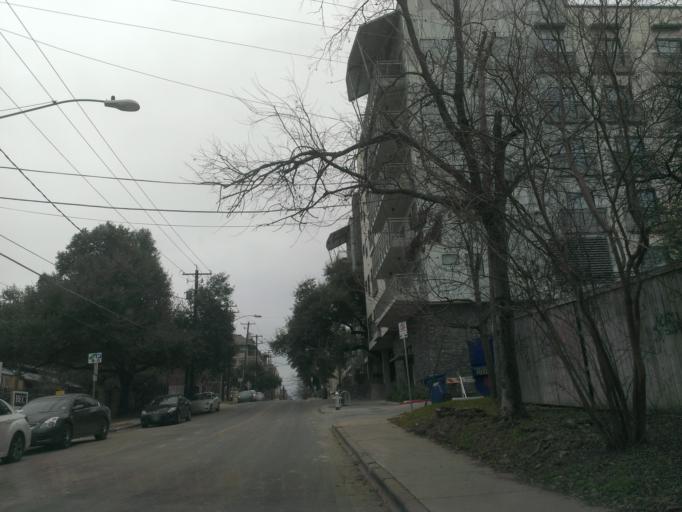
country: US
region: Texas
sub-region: Travis County
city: Austin
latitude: 30.2909
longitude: -97.7487
